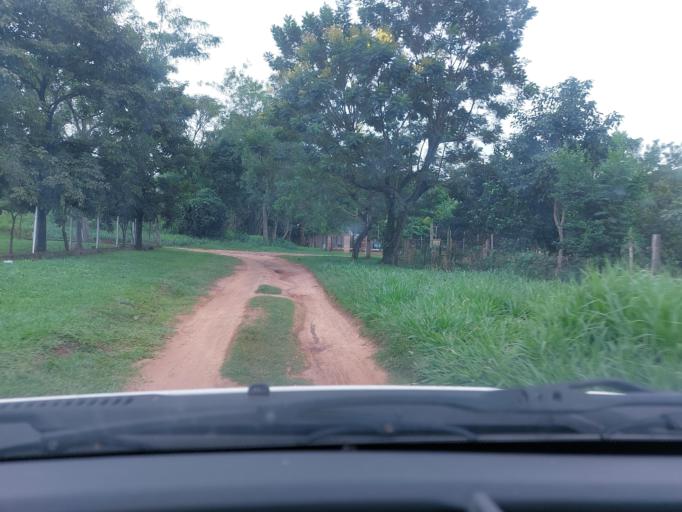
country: PY
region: San Pedro
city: Guayaybi
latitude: -24.6792
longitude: -56.4468
